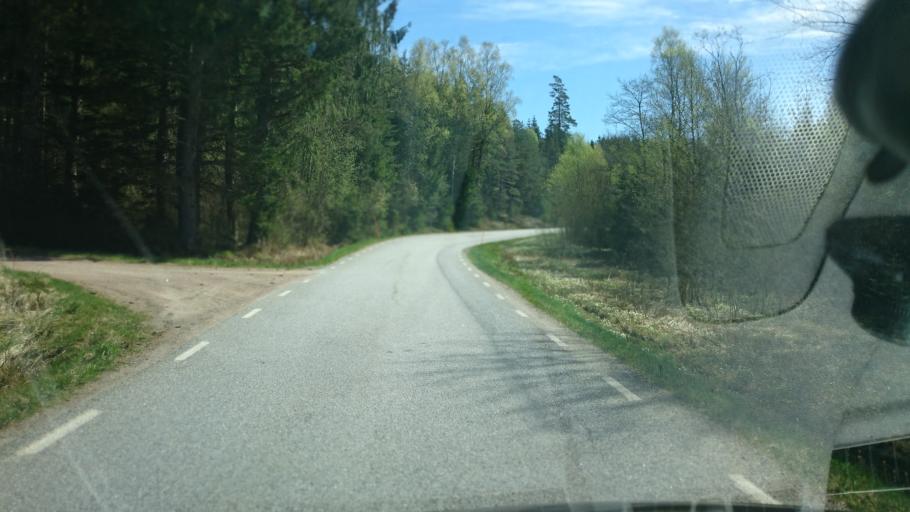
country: SE
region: Vaestra Goetaland
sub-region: Munkedals Kommun
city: Munkedal
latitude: 58.3693
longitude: 11.6925
